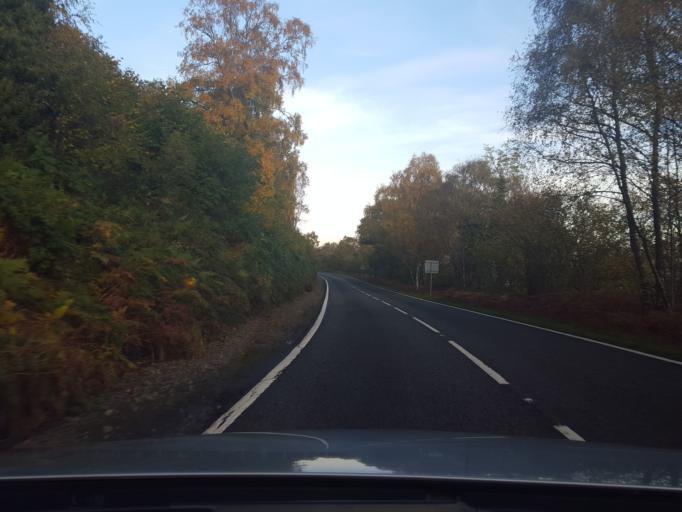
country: GB
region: Scotland
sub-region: Highland
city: Beauly
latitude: 57.3607
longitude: -4.3964
